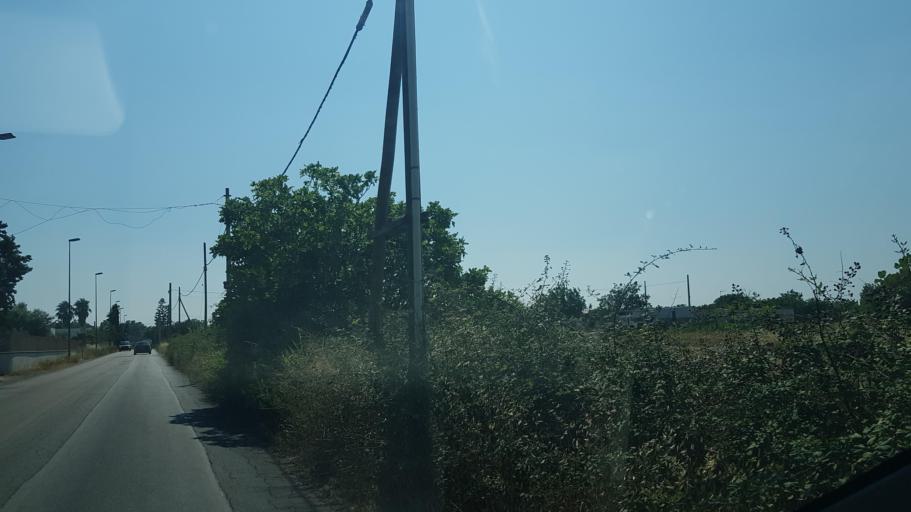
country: IT
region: Apulia
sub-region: Provincia di Lecce
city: Taurisano
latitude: 39.9539
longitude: 18.2061
